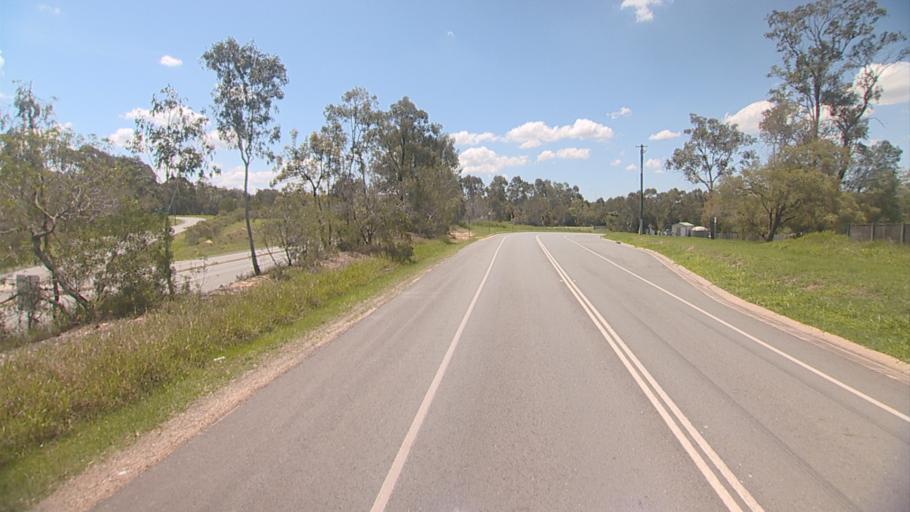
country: AU
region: Queensland
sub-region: Logan
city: Park Ridge South
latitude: -27.7271
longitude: 153.0301
